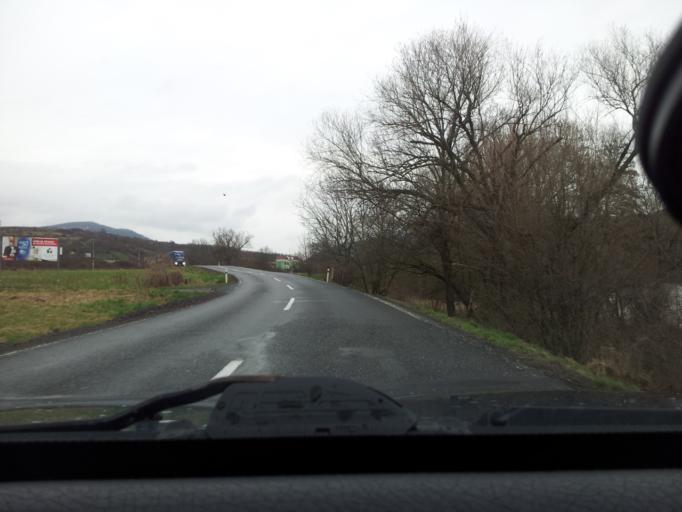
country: SK
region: Nitriansky
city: Tlmace
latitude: 48.3246
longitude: 18.5461
